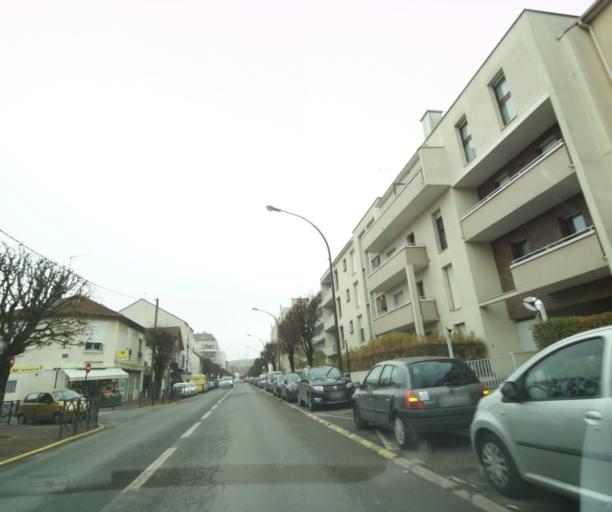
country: FR
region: Ile-de-France
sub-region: Departement de Seine-Saint-Denis
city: Livry-Gargan
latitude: 48.9289
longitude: 2.5417
